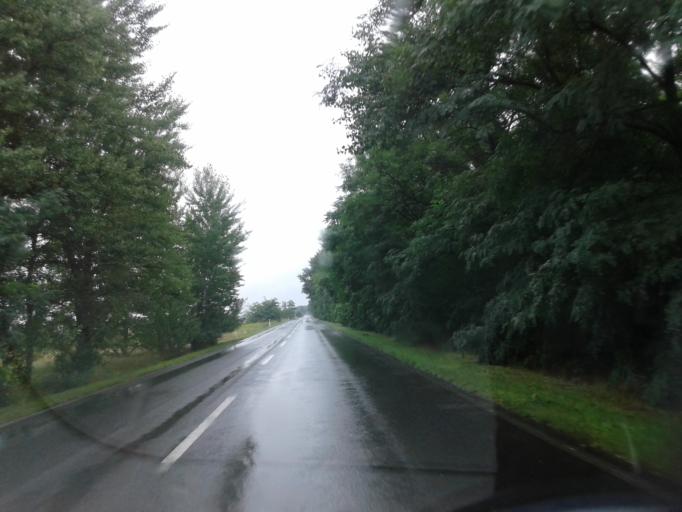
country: HU
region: Csongrad
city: Ruzsa
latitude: 46.2449
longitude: 19.6947
